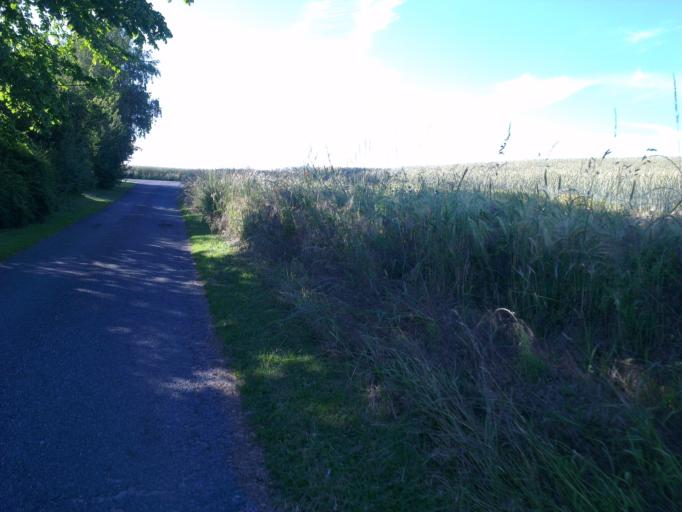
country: DK
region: Capital Region
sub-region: Frederikssund Kommune
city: Skibby
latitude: 55.7517
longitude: 12.0354
